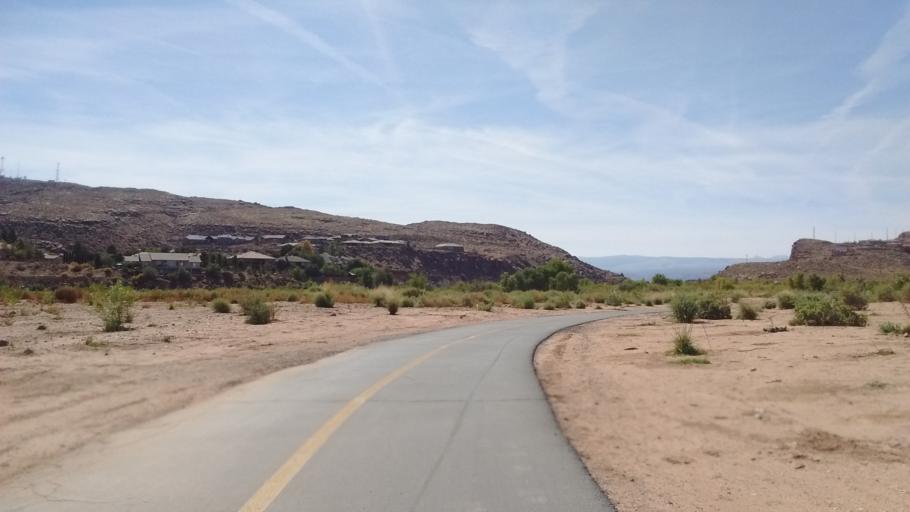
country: US
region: Utah
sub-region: Washington County
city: Saint George
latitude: 37.0770
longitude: -113.5779
